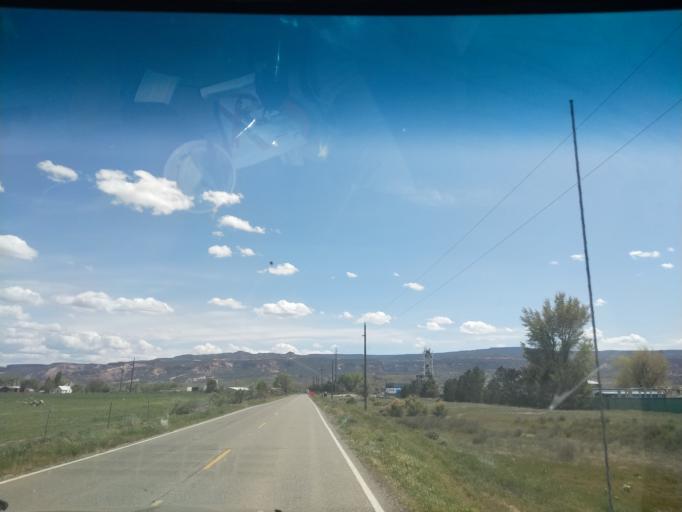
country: US
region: Colorado
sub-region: Mesa County
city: Fruita
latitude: 39.1713
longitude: -108.7571
